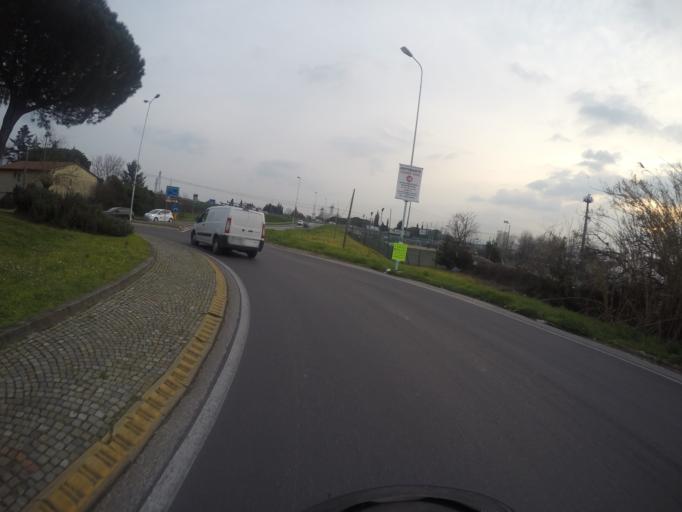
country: IT
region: Tuscany
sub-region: Province of Florence
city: Campi Bisenzio
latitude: 43.8553
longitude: 11.1235
